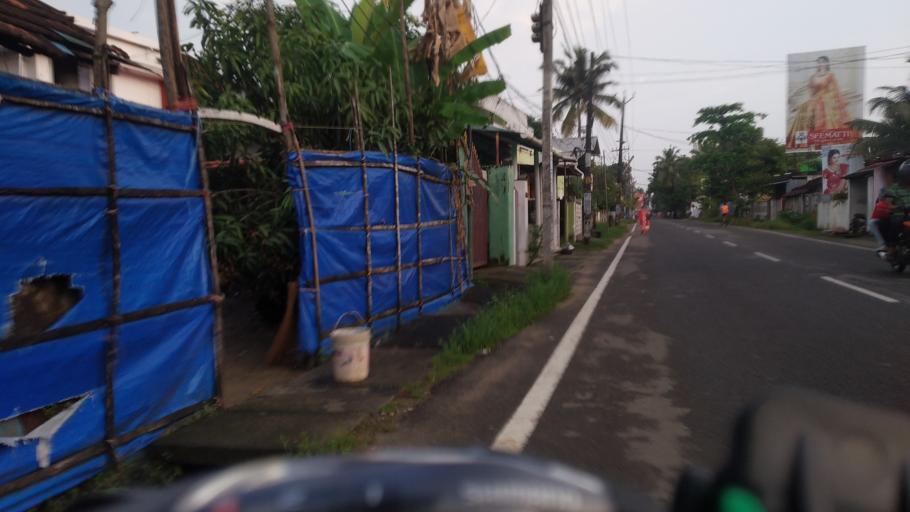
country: IN
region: Kerala
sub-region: Ernakulam
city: Cochin
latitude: 9.9788
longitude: 76.2409
